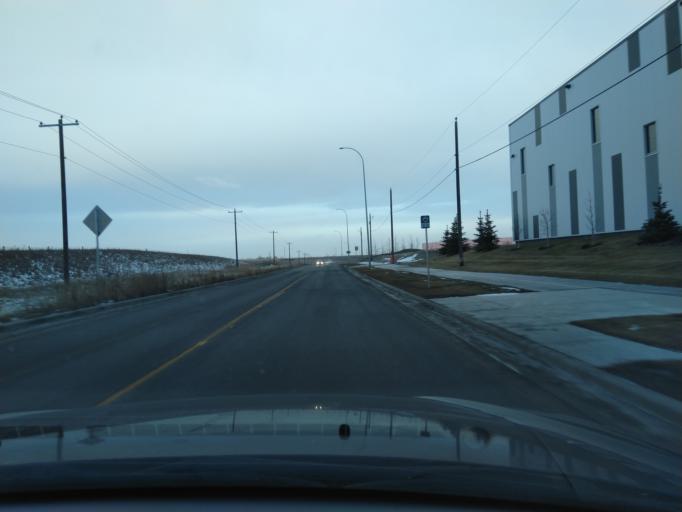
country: CA
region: Alberta
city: Calgary
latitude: 51.1622
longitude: -114.0248
